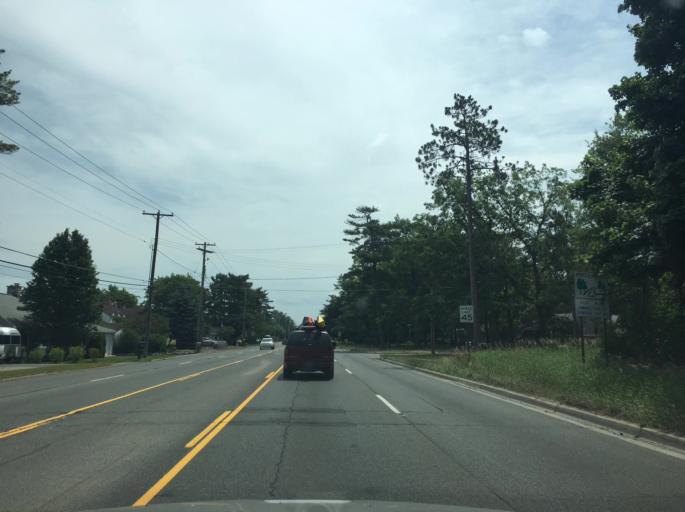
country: US
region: Michigan
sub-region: Grand Traverse County
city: Traverse City
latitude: 44.7535
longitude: -85.5695
